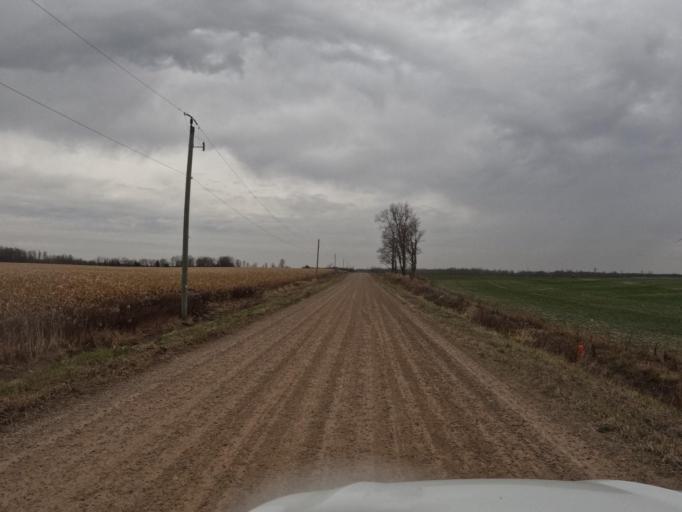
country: CA
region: Ontario
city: Shelburne
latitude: 43.8857
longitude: -80.3821
